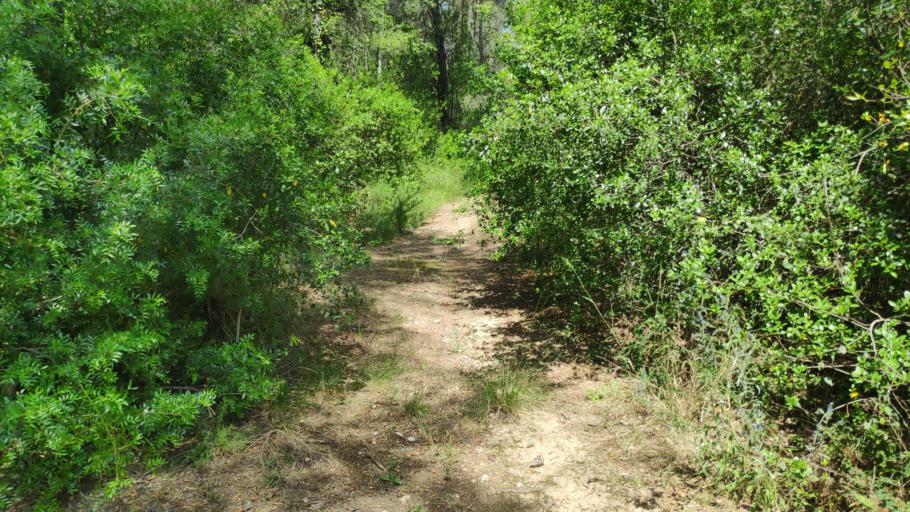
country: ES
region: Catalonia
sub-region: Provincia de Barcelona
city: Rubi
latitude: 41.5009
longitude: 2.0605
